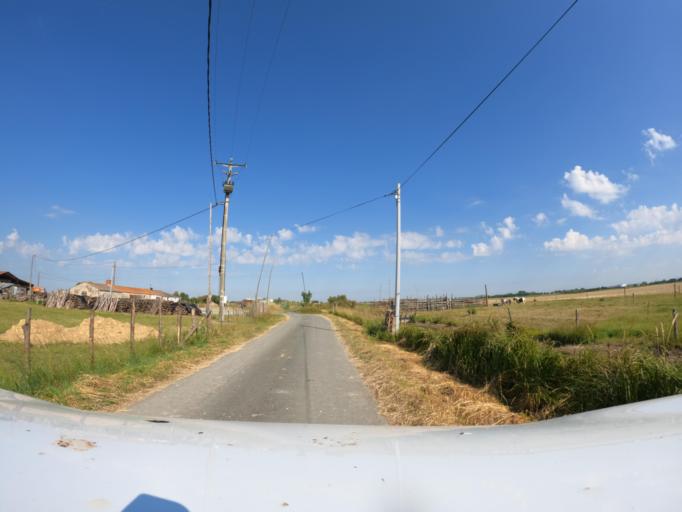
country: FR
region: Pays de la Loire
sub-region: Departement de la Vendee
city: Champagne-les-Marais
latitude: 46.3638
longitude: -1.1164
